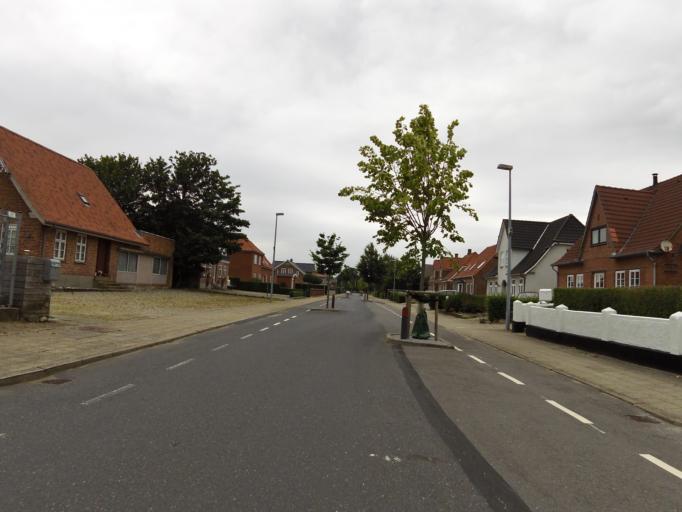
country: DK
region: South Denmark
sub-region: Tonder Kommune
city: Logumkloster
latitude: 55.0732
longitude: 8.9319
